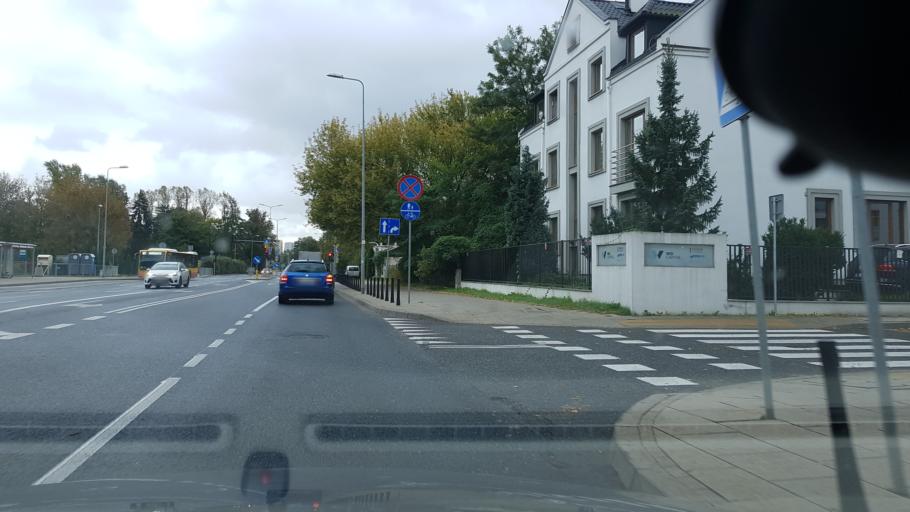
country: PL
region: Masovian Voivodeship
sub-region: Warszawa
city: Zoliborz
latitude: 52.2882
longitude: 20.9760
